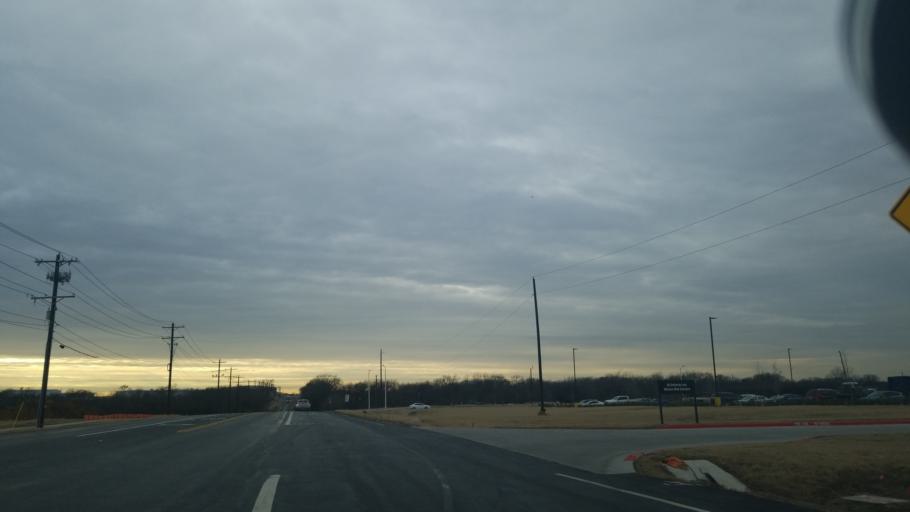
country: US
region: Texas
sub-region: Denton County
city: Denton
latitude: 33.2018
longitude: -97.1837
